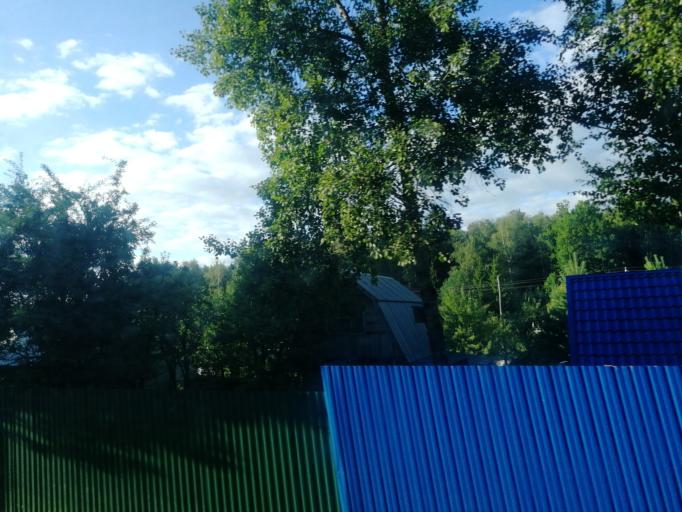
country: RU
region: Kaluga
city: Kaluga
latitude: 54.4522
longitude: 36.2957
